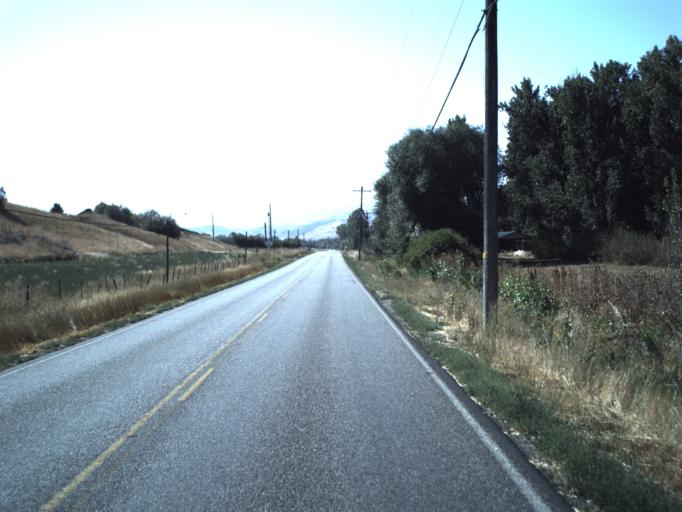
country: US
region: Utah
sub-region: Cache County
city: Hyrum
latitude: 41.5928
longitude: -111.8369
